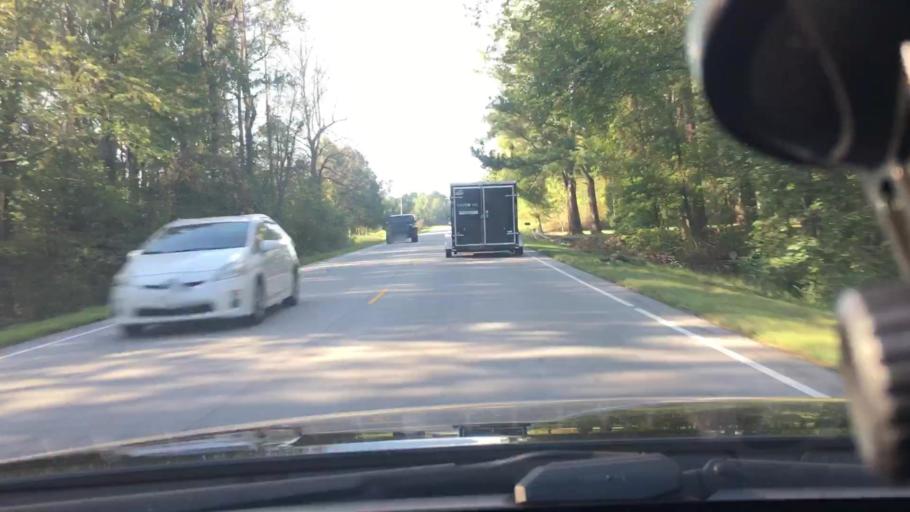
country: US
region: North Carolina
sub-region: Craven County
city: Vanceboro
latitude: 35.3139
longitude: -77.1409
